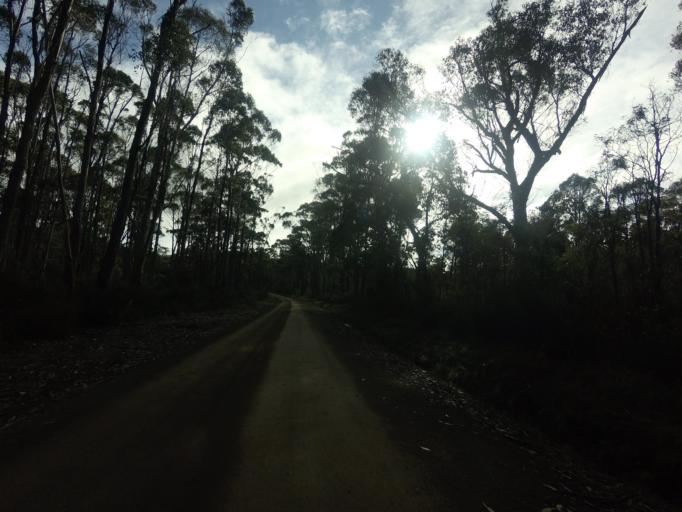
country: AU
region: Tasmania
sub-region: Derwent Valley
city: New Norfolk
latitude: -42.7693
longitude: 146.9003
